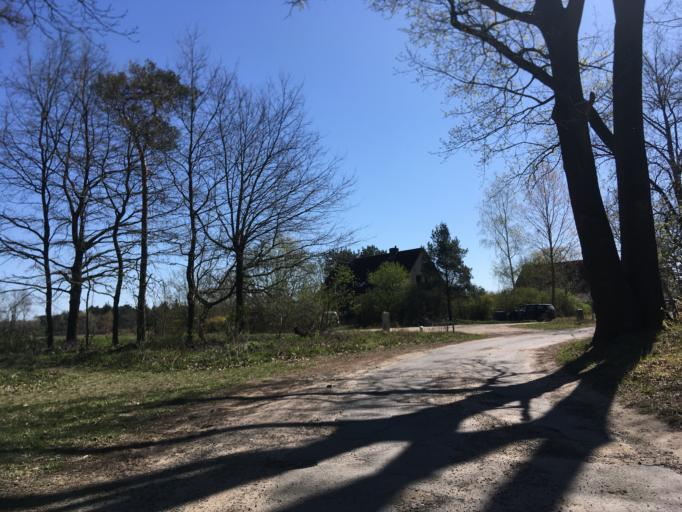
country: DE
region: Berlin
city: Buch
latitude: 52.6805
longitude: 13.4759
